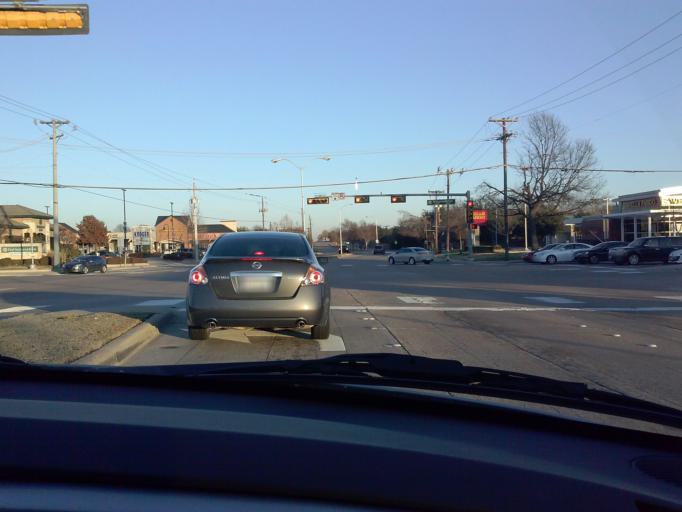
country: US
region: Texas
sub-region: Collin County
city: Plano
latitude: 33.0718
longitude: -96.7506
